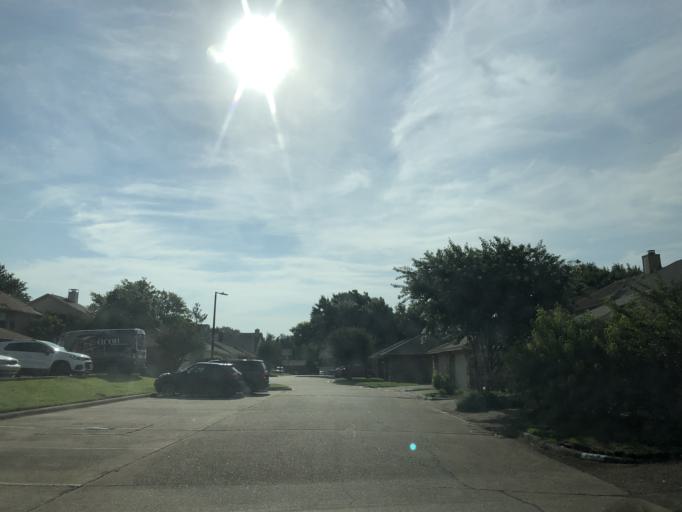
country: US
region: Texas
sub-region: Dallas County
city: Sunnyvale
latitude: 32.8406
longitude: -96.6150
